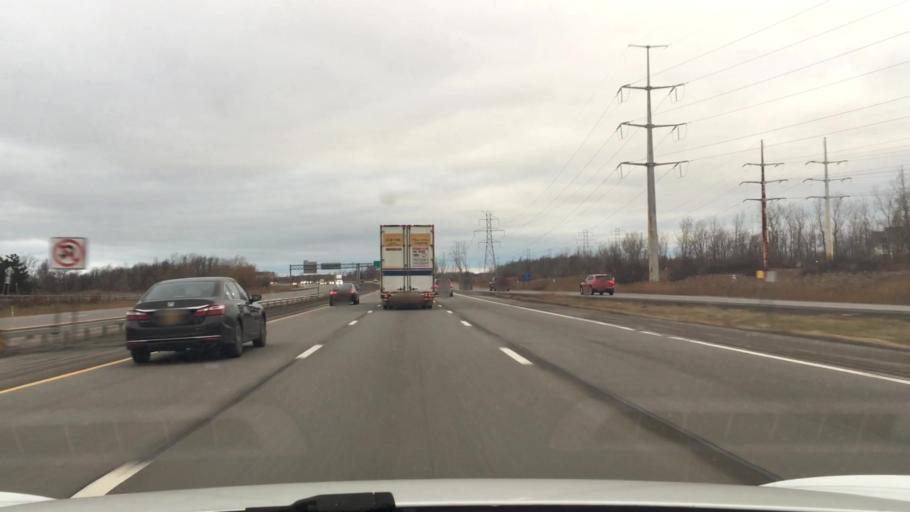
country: US
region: New York
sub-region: Erie County
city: Amherst
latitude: 42.9993
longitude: -78.8102
